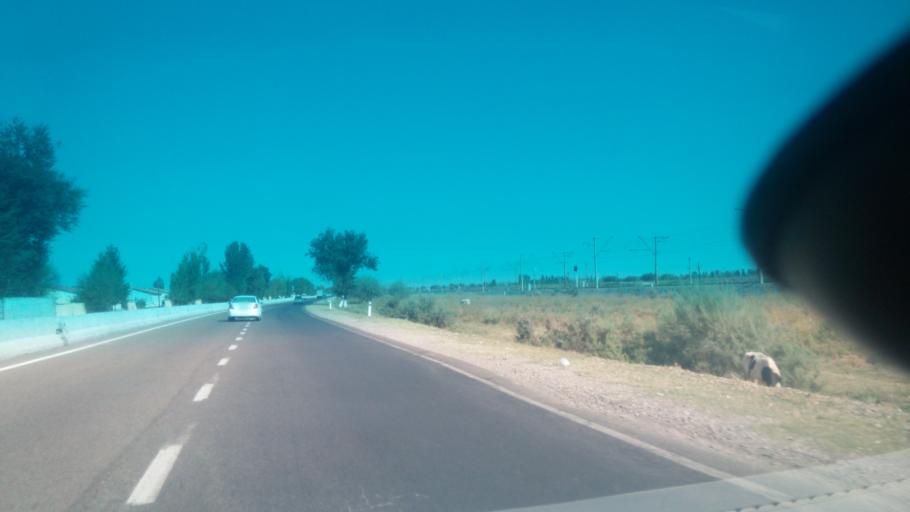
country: UZ
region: Sirdaryo
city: Sirdaryo
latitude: 40.7503
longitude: 68.6862
